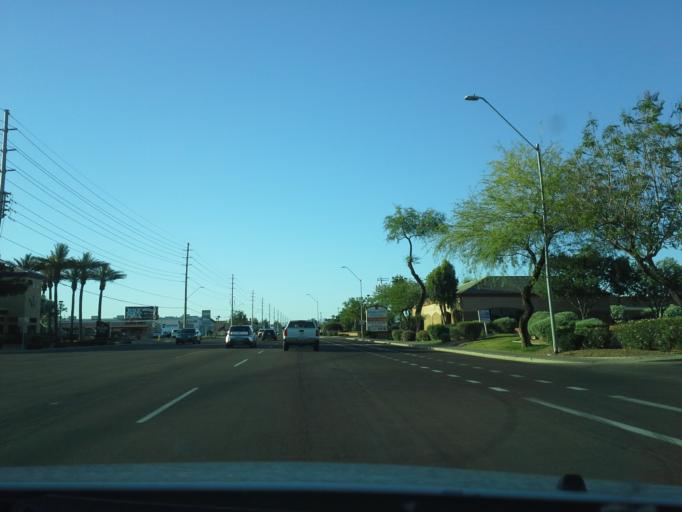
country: US
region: Arizona
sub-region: Maricopa County
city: Paradise Valley
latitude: 33.6271
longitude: -112.0133
